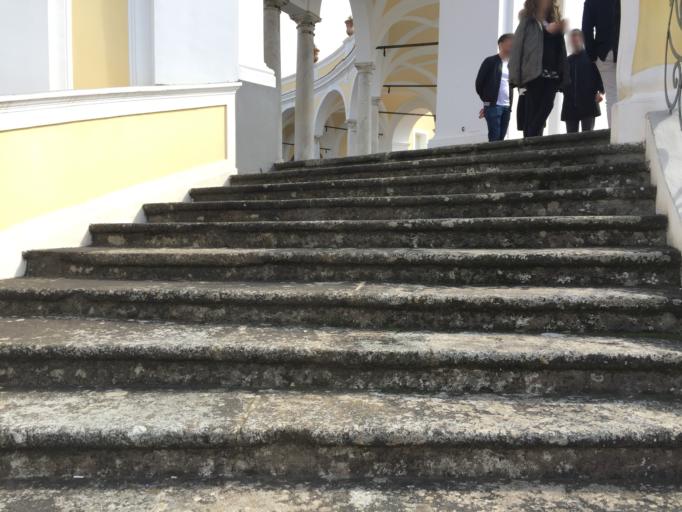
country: IT
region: Campania
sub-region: Provincia di Napoli
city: Ercolano
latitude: 40.8011
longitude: 14.3526
